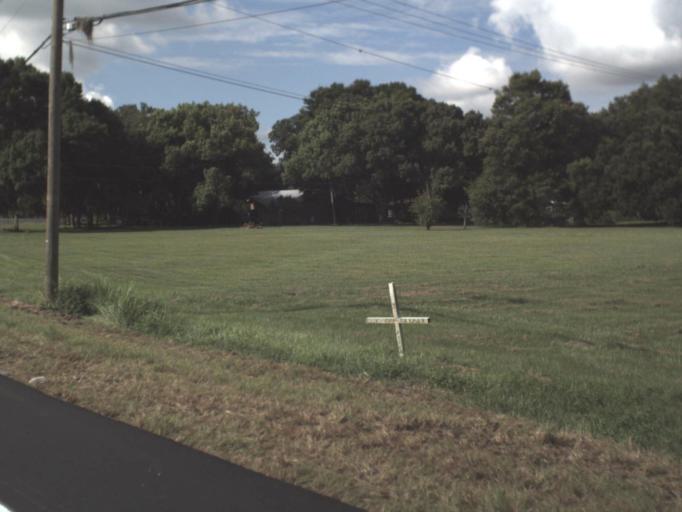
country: US
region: Florida
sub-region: Polk County
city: Combee Settlement
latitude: 28.0856
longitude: -81.9057
